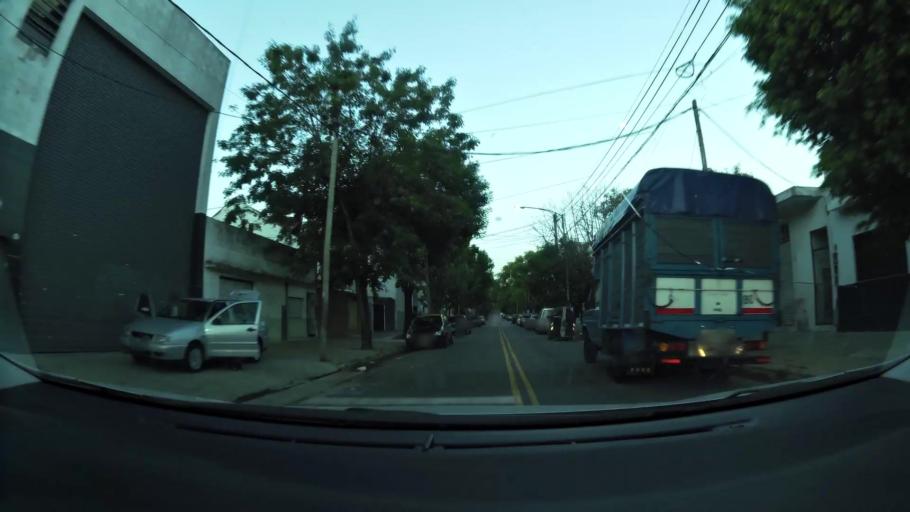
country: AR
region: Buenos Aires F.D.
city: Villa Lugano
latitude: -34.6811
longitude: -58.4698
